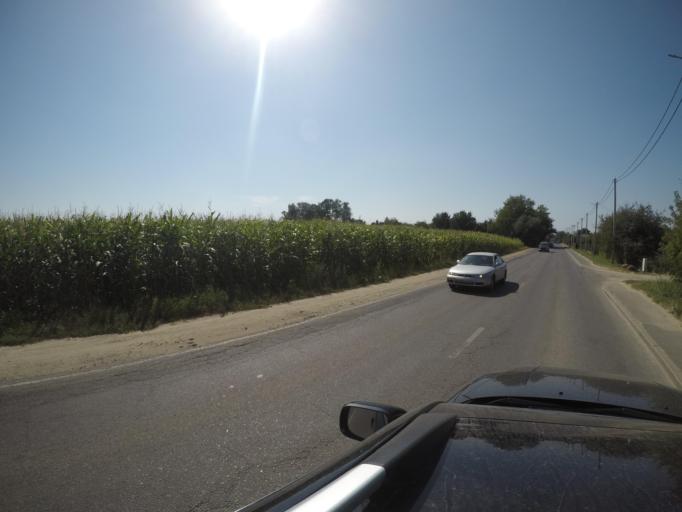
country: BY
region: Grodnenskaya
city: Hrodna
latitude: 53.7096
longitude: 23.8680
